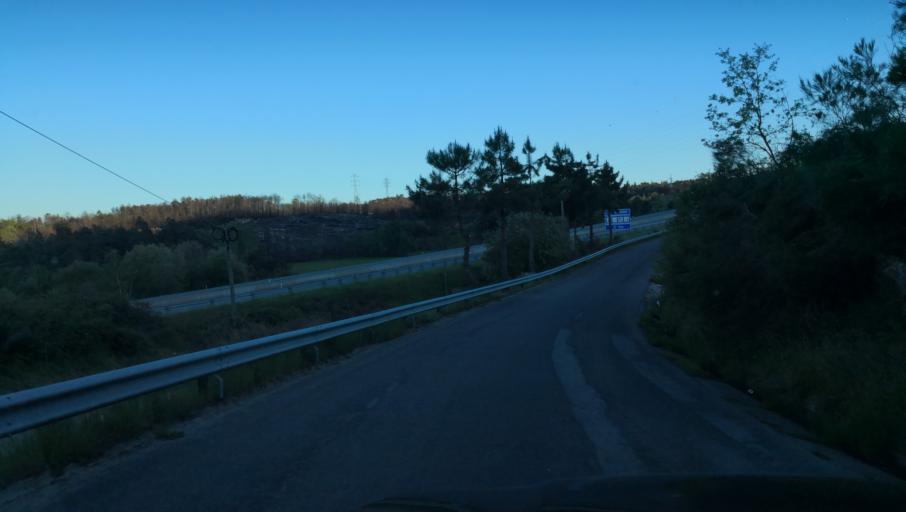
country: PT
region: Vila Real
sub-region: Sabrosa
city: Sabrosa
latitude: 41.3380
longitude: -7.6228
